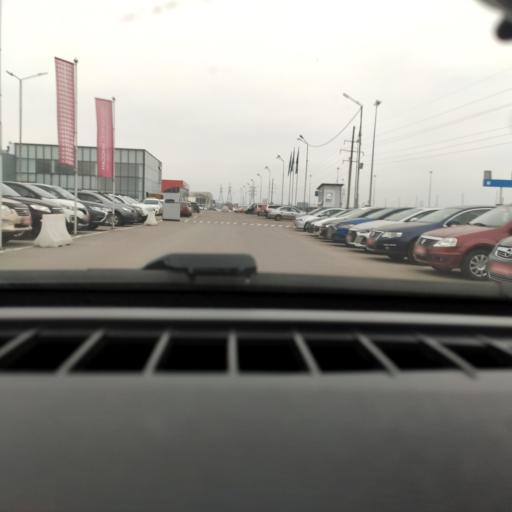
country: RU
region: Voronezj
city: Somovo
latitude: 51.6619
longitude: 39.3028
